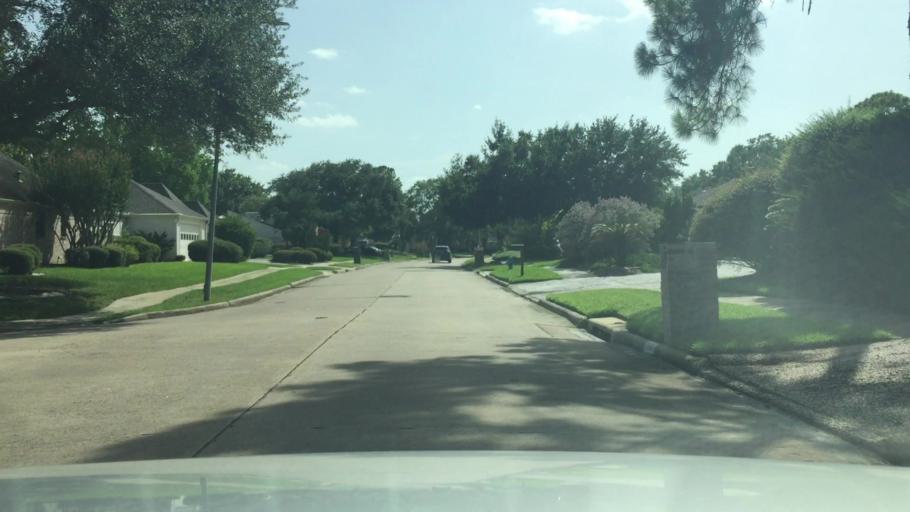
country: US
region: Texas
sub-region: Harris County
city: Bunker Hill Village
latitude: 29.7543
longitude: -95.5782
